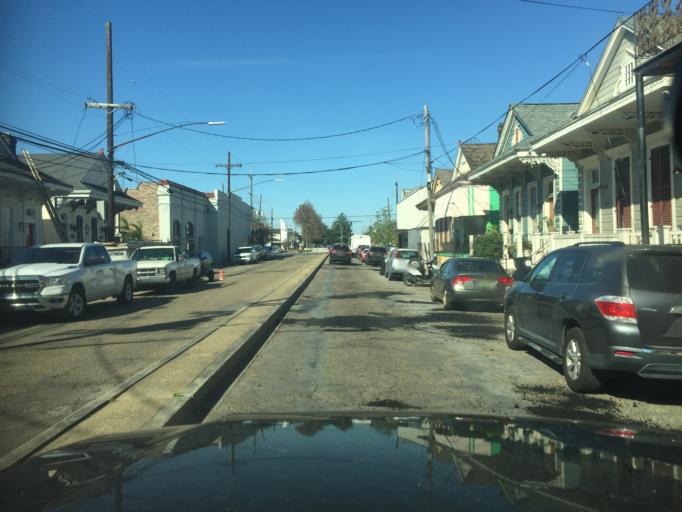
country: US
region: Louisiana
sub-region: Orleans Parish
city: New Orleans
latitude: 29.9407
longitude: -90.0783
